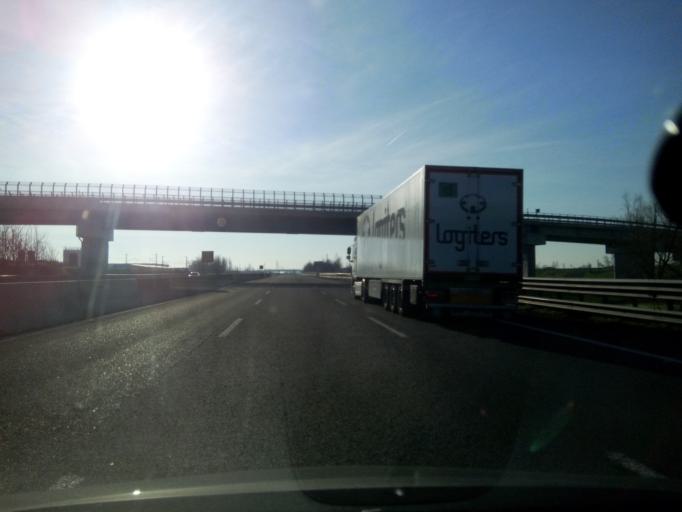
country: IT
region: Emilia-Romagna
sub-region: Provincia di Reggio Emilia
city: Praticello
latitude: 44.8020
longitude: 10.4454
